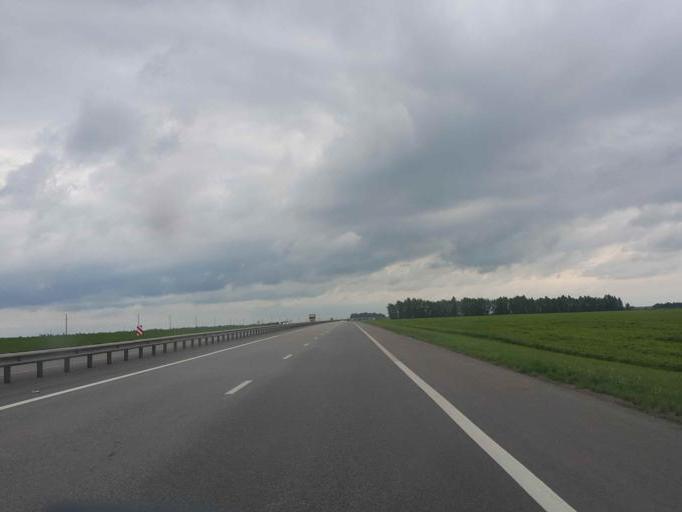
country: RU
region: Tambov
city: Zavoronezhskoye
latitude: 52.8307
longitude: 40.8873
